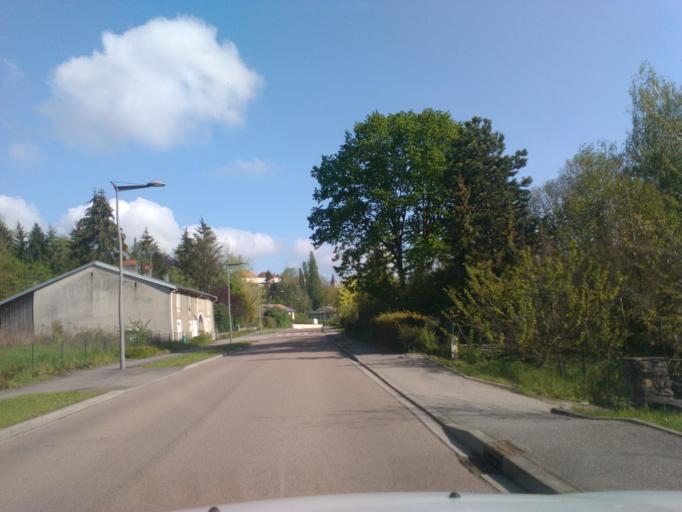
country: FR
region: Lorraine
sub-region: Departement des Vosges
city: Mirecourt
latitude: 48.3163
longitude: 6.1258
